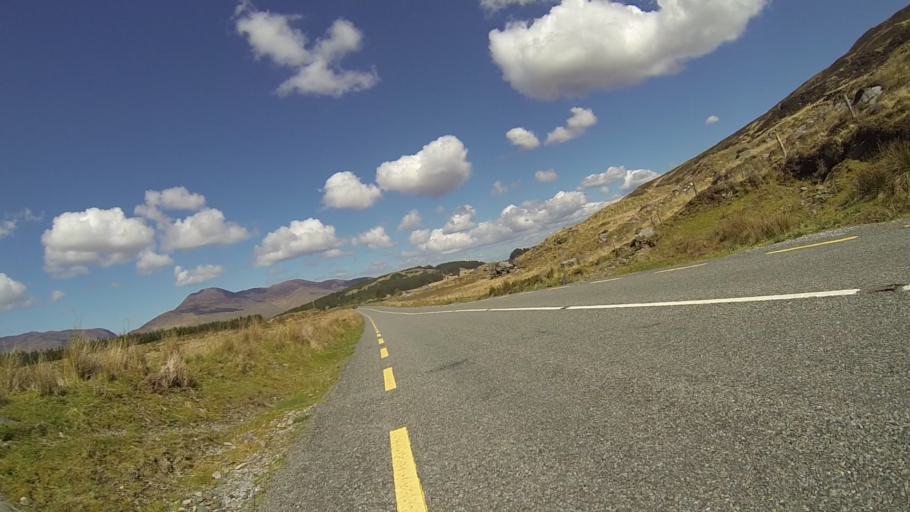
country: IE
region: Munster
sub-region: Ciarrai
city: Kenmare
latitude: 51.9503
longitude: -9.6276
